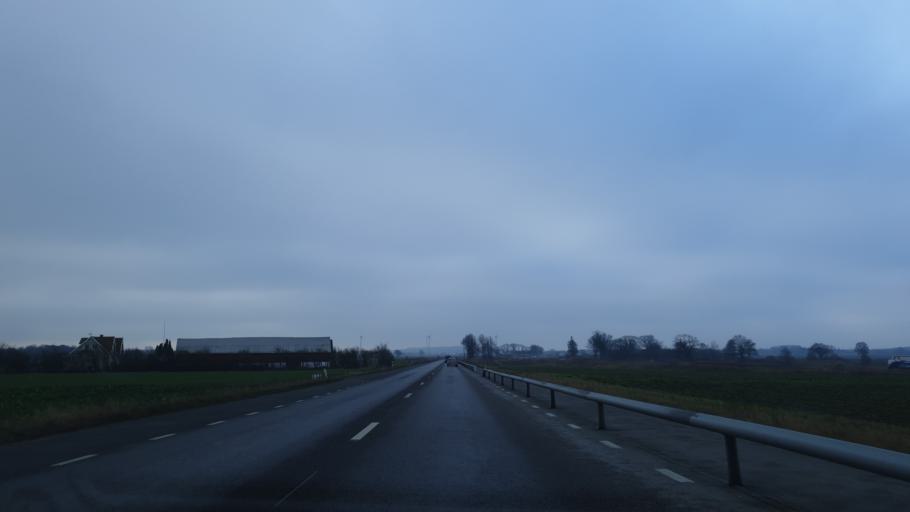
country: SE
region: Blekinge
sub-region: Solvesborgs Kommun
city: Soelvesborg
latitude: 56.0837
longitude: 14.6463
